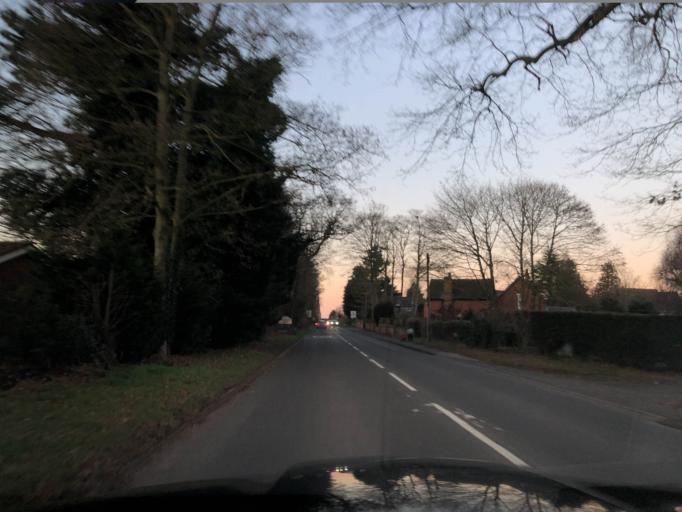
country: GB
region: England
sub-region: Warwickshire
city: Kenilworth
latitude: 52.3306
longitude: -1.5740
